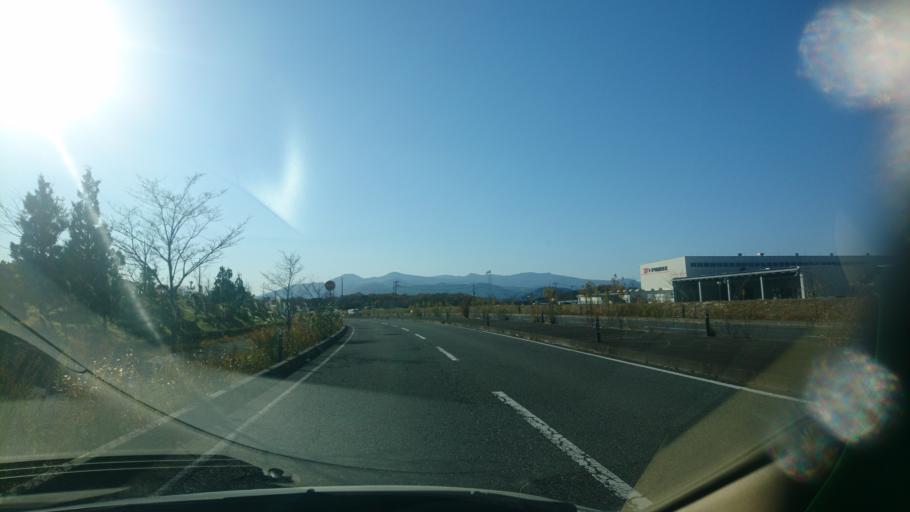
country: JP
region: Miyagi
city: Tomiya
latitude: 38.4740
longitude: 140.8947
